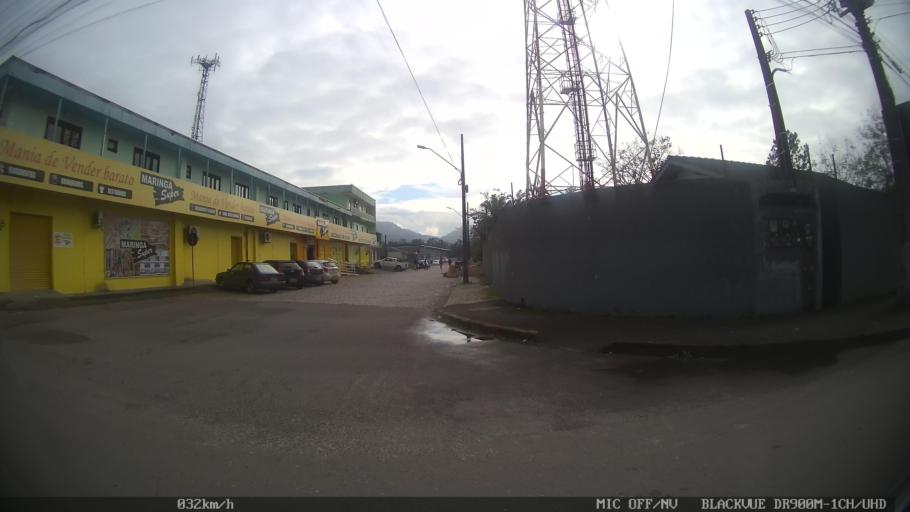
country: BR
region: Santa Catarina
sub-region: Joinville
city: Joinville
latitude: -26.0294
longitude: -48.8566
